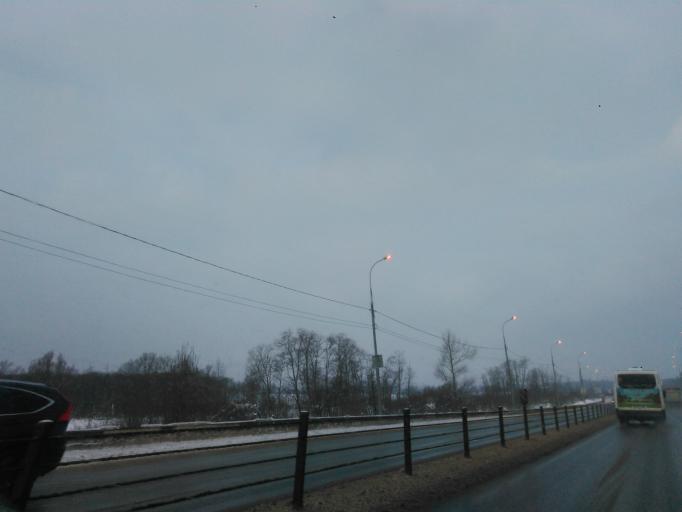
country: RU
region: Moskovskaya
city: Podosinki
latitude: 56.2146
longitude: 37.5217
